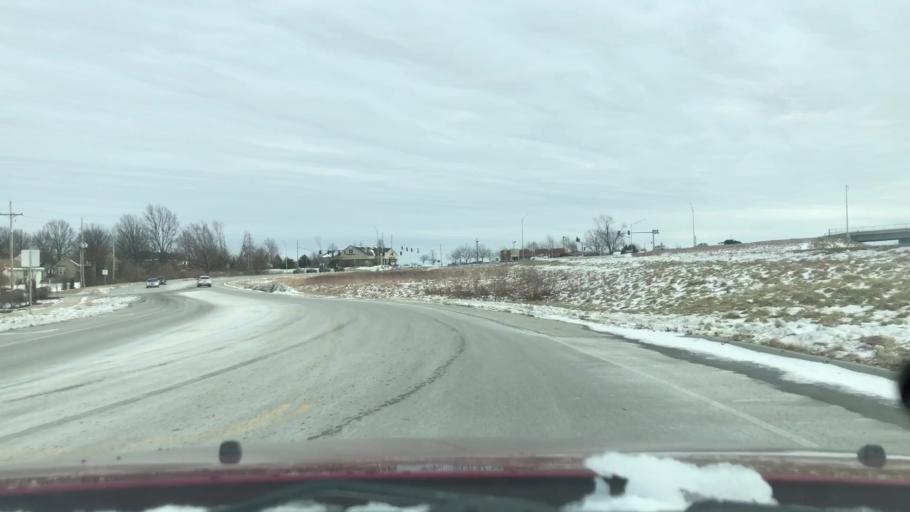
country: US
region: Missouri
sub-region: Jackson County
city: Lees Summit
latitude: 38.9028
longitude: -94.3427
